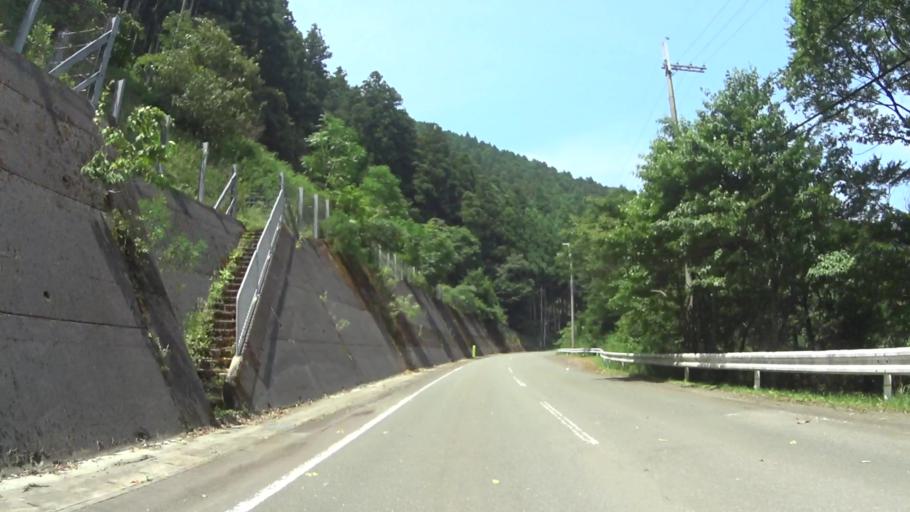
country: JP
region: Kyoto
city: Ayabe
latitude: 35.2956
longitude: 135.4277
